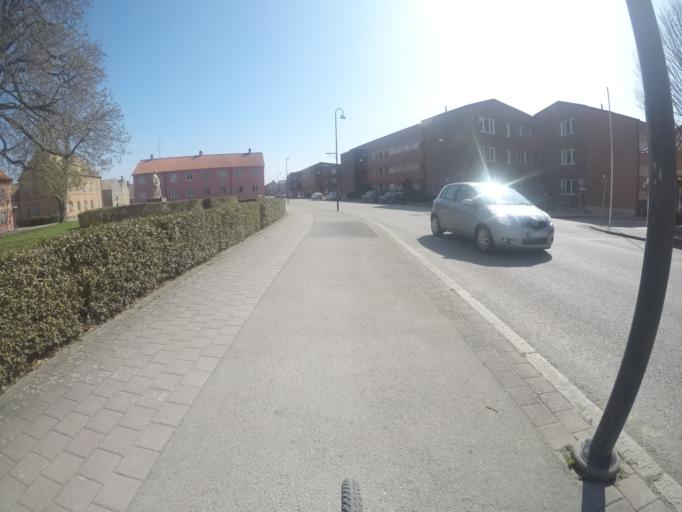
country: SE
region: Skane
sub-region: Hoganas Kommun
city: Hoganas
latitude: 56.1998
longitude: 12.5727
